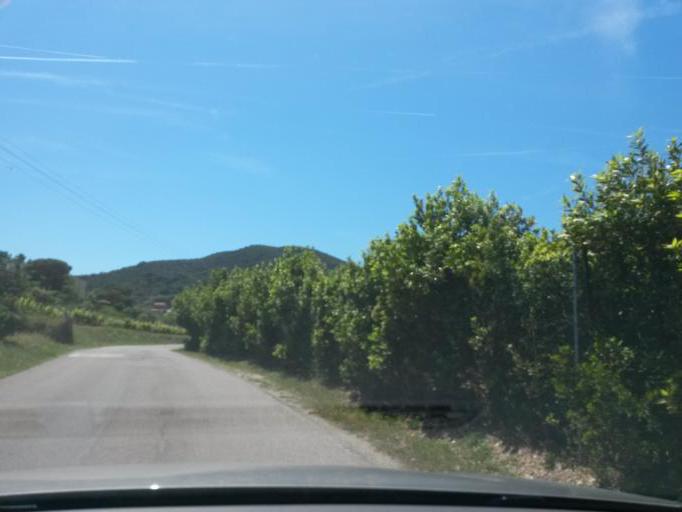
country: IT
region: Tuscany
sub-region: Provincia di Livorno
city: Portoferraio
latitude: 42.8180
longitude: 10.3059
